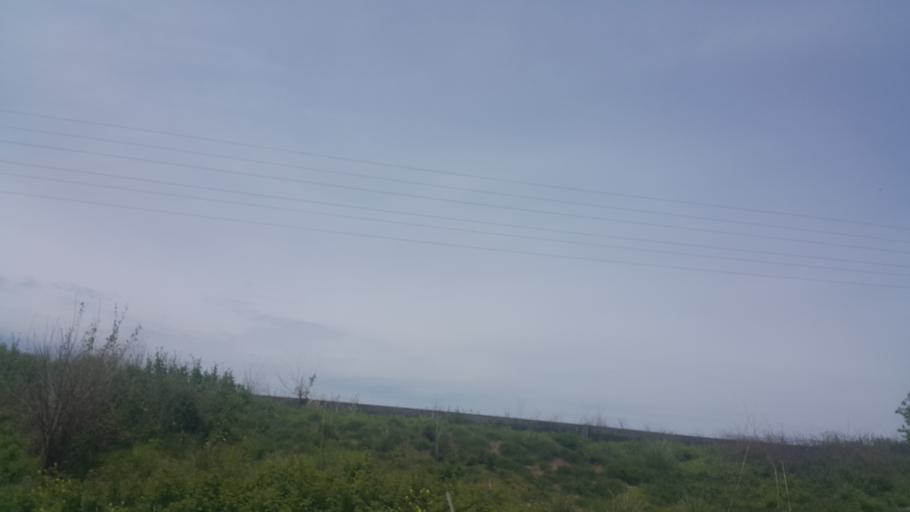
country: TR
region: Adana
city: Kosreli
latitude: 37.0708
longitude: 36.0195
